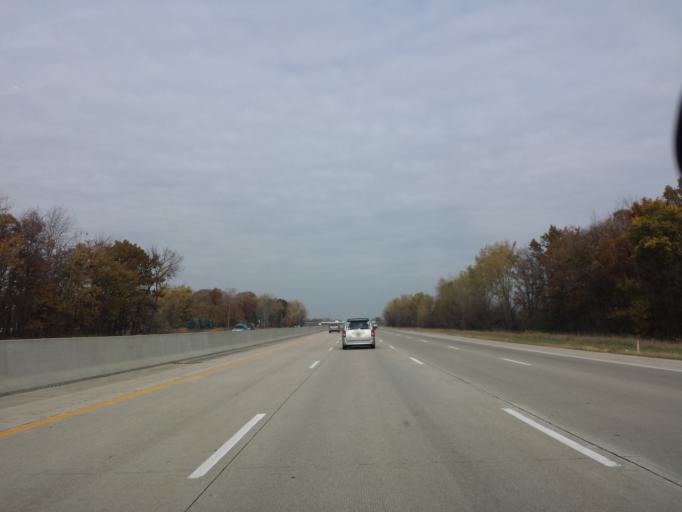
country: US
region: Michigan
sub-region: Bay County
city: Bay City
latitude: 43.5868
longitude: -83.9485
